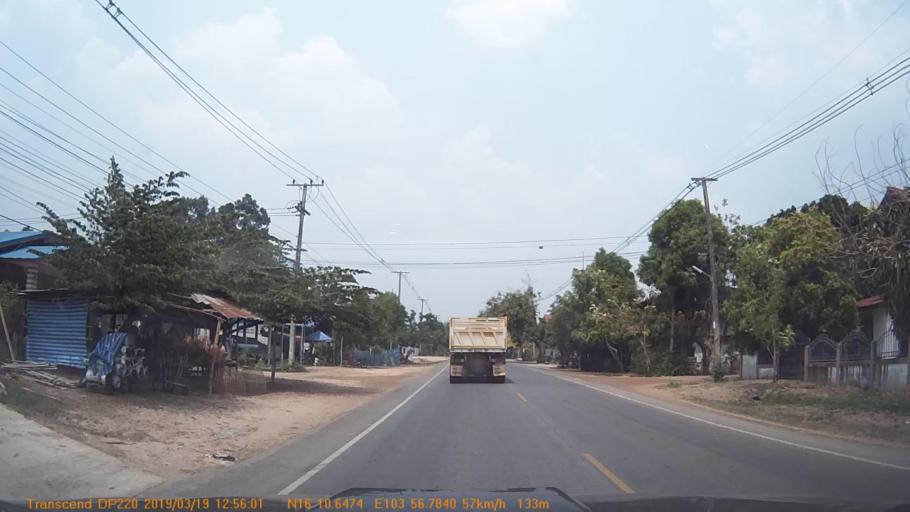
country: TH
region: Roi Et
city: Waeng
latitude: 16.1776
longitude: 103.9464
